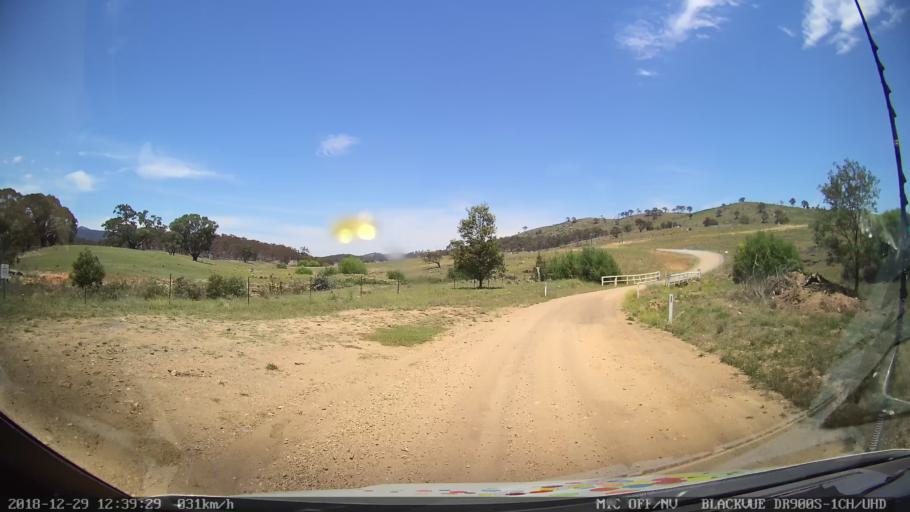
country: AU
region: Australian Capital Territory
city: Macarthur
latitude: -35.5972
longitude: 149.2272
